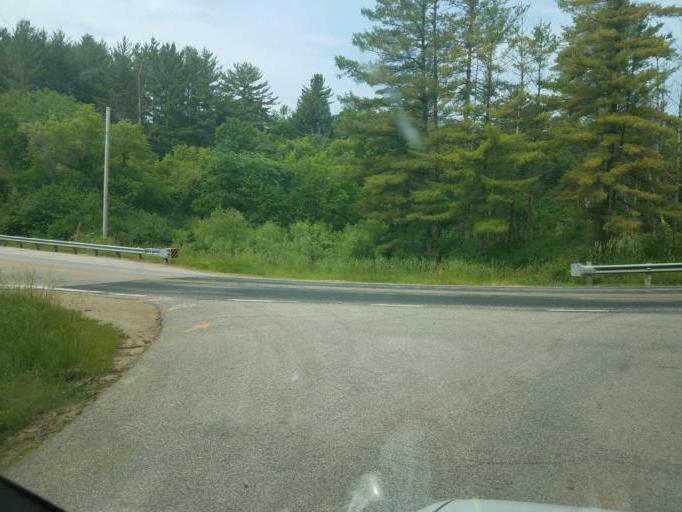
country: US
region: Wisconsin
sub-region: Monroe County
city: Cashton
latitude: 43.7113
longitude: -90.5812
